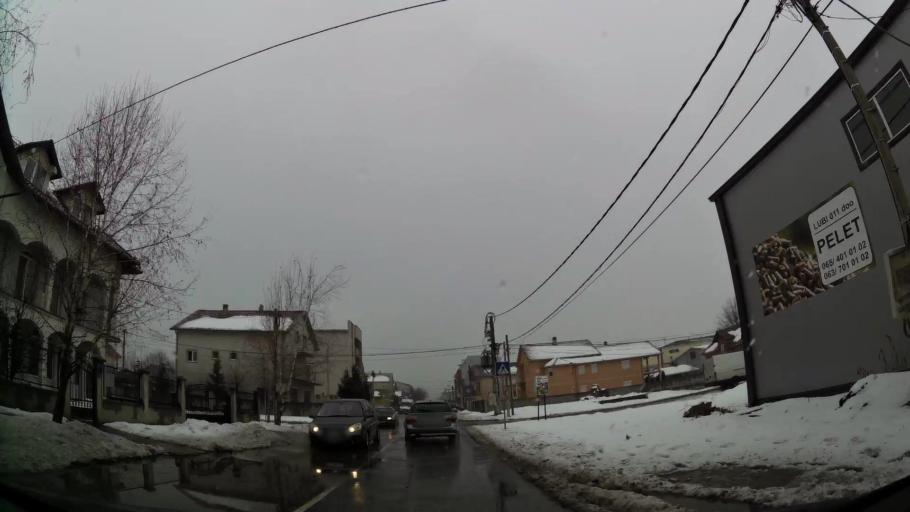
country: RS
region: Central Serbia
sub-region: Belgrade
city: Zemun
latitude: 44.8541
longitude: 20.3457
